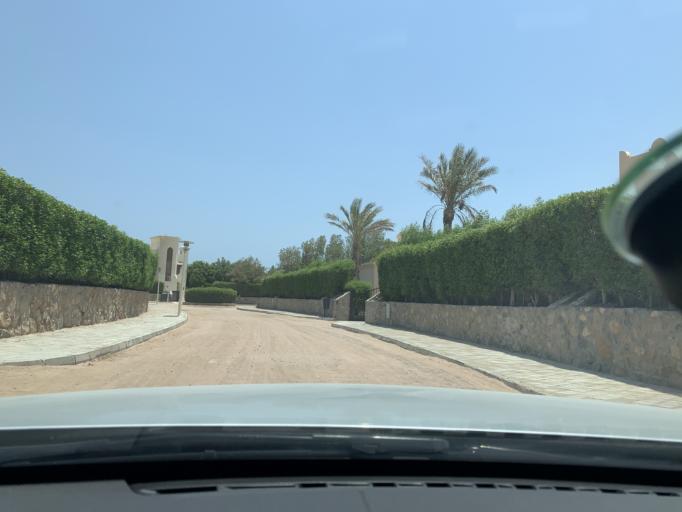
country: EG
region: Red Sea
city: El Gouna
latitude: 27.4140
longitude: 33.6698
